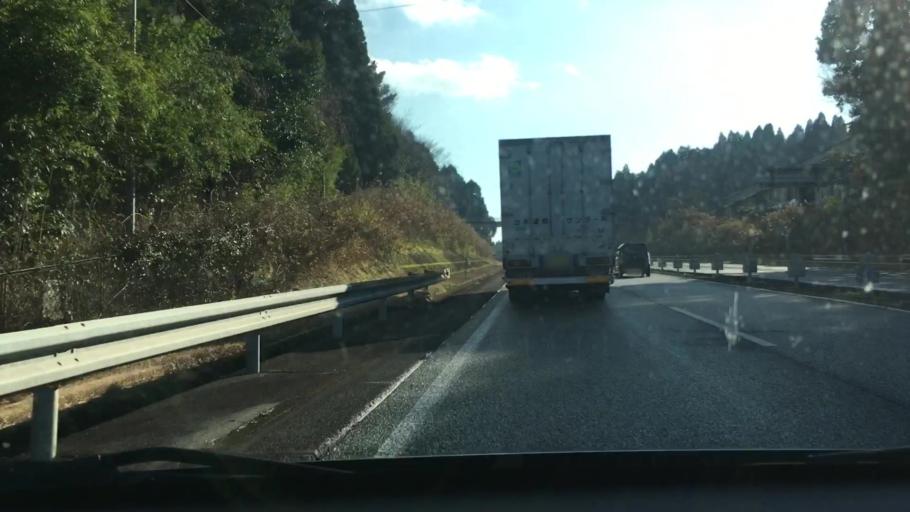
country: JP
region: Kagoshima
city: Okuchi-shinohara
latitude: 31.9301
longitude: 130.7052
